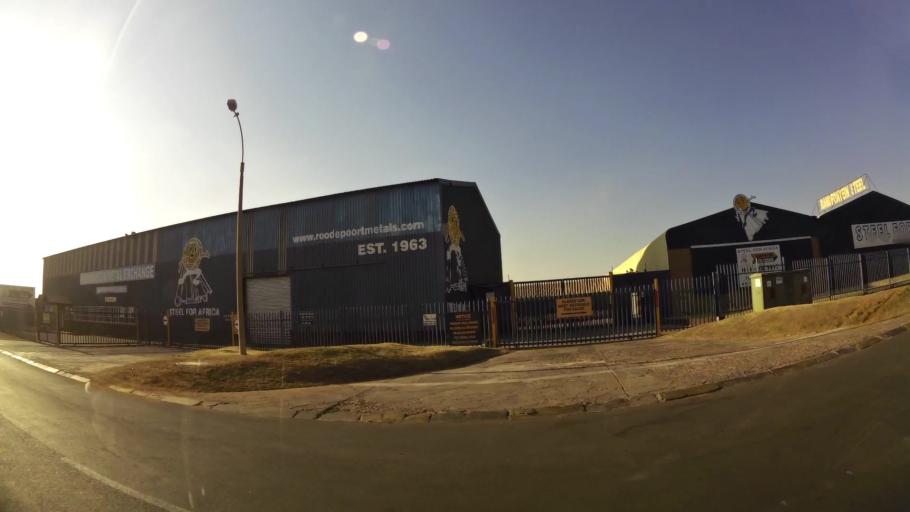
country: ZA
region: Gauteng
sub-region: West Rand District Municipality
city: Randfontein
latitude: -26.1998
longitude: 27.6953
